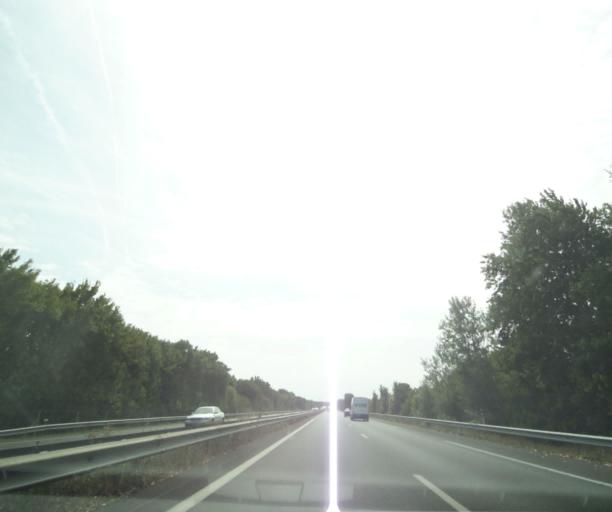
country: FR
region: Poitou-Charentes
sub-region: Departement de la Charente-Maritime
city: Saint-Jean-d'Angely
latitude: 46.0700
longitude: -0.5331
